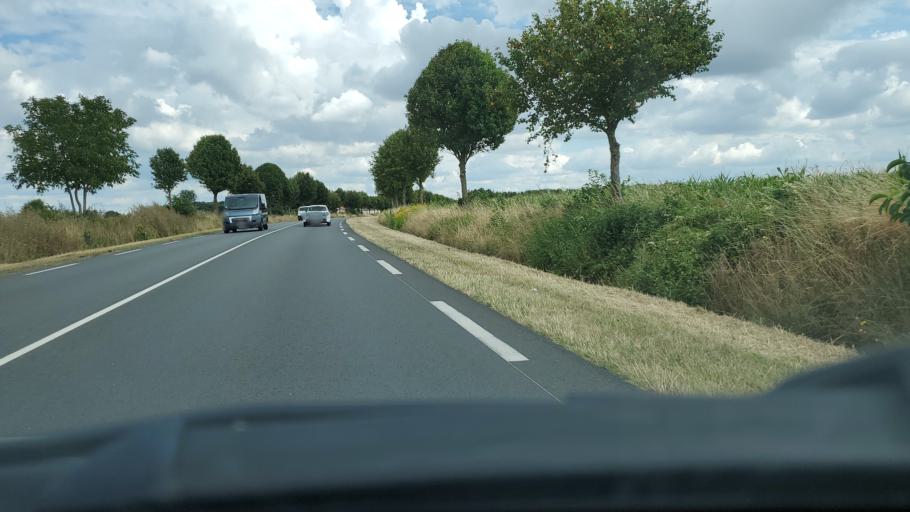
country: FR
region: Ile-de-France
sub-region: Departement de Seine-et-Marne
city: Nanteuil-les-Meaux
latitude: 48.9138
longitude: 2.9142
